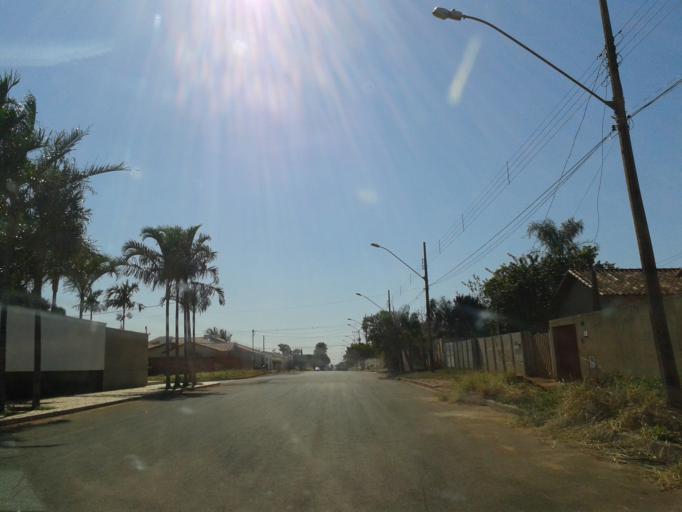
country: BR
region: Minas Gerais
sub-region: Ituiutaba
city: Ituiutaba
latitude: -18.9936
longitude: -49.4595
